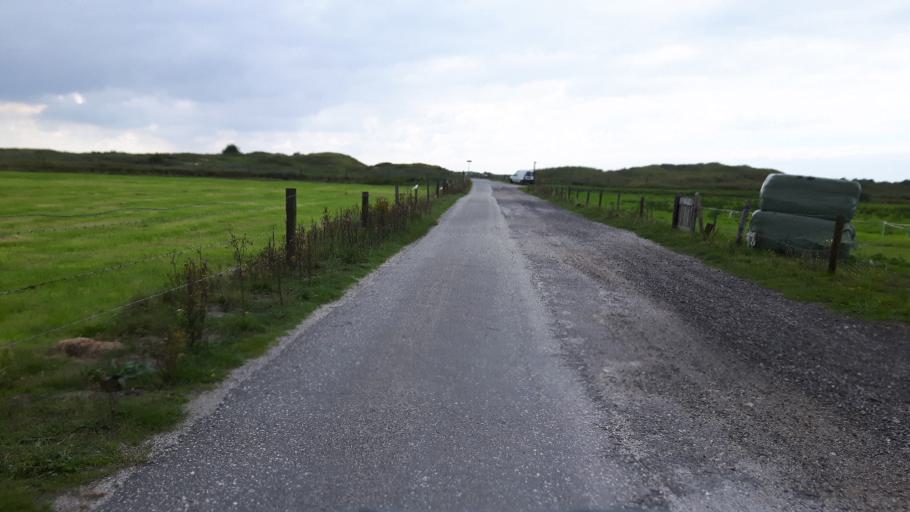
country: NL
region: Friesland
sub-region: Gemeente Ameland
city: Nes
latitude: 53.4549
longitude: 5.8222
